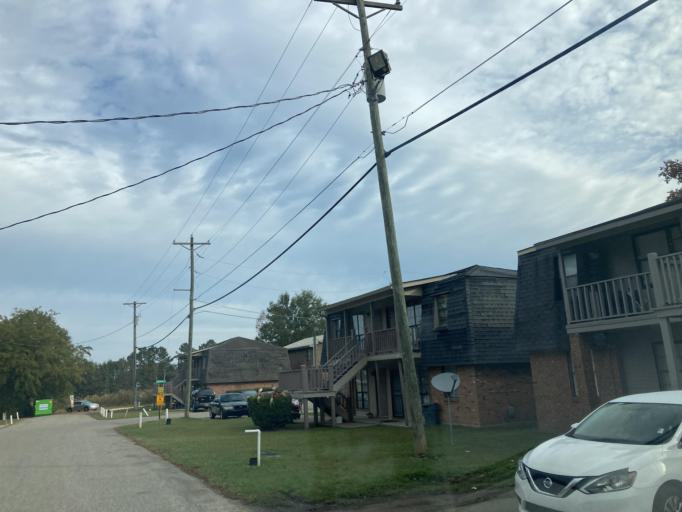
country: US
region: Mississippi
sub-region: Lamar County
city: West Hattiesburg
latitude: 31.3191
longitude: -89.3706
